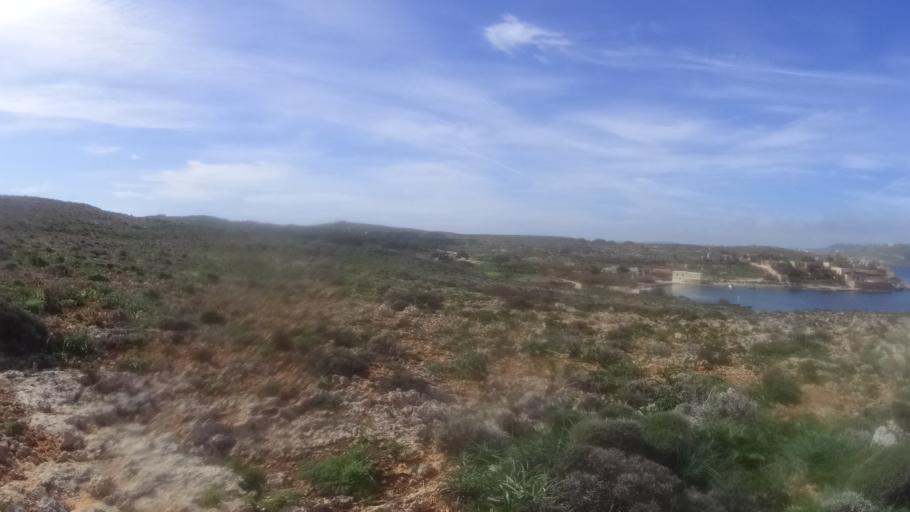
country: MT
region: Il-Qala
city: Qala
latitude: 36.0162
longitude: 14.3399
